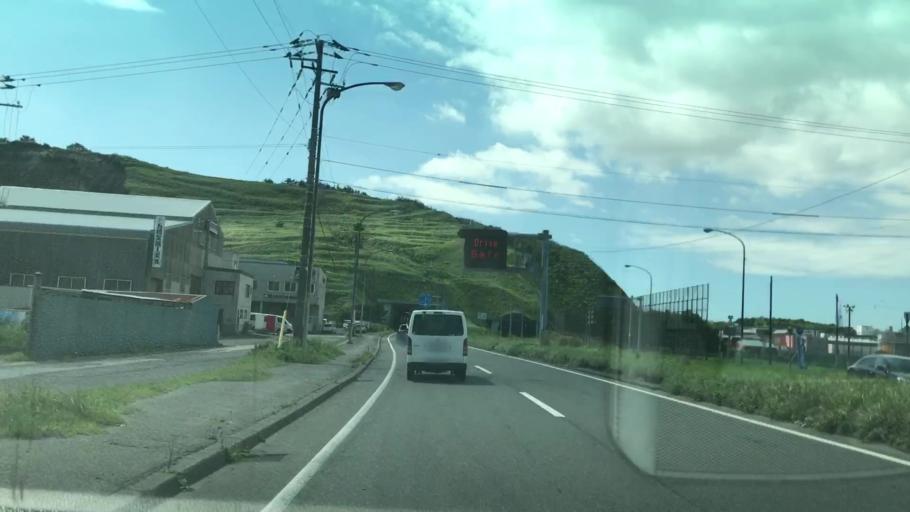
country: JP
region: Hokkaido
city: Muroran
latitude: 42.3434
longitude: 141.0342
